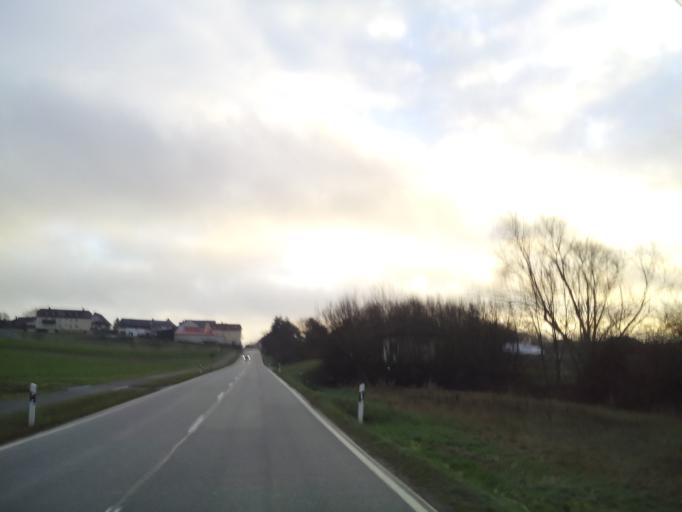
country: DE
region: Bavaria
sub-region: Upper Franconia
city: Untersiemau
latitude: 50.1853
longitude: 11.0043
